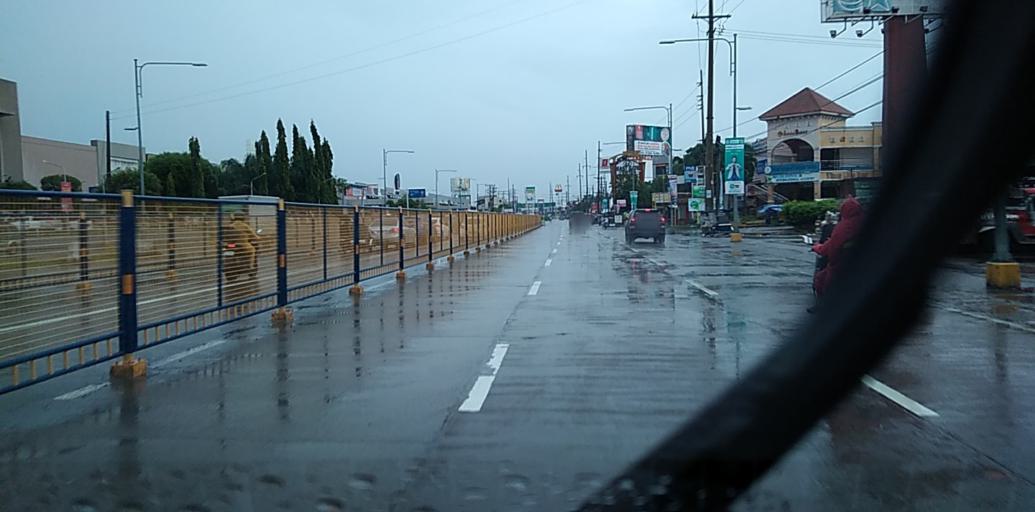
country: PH
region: Central Luzon
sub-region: Province of Pampanga
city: Del Pilar
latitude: 15.0513
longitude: 120.6988
